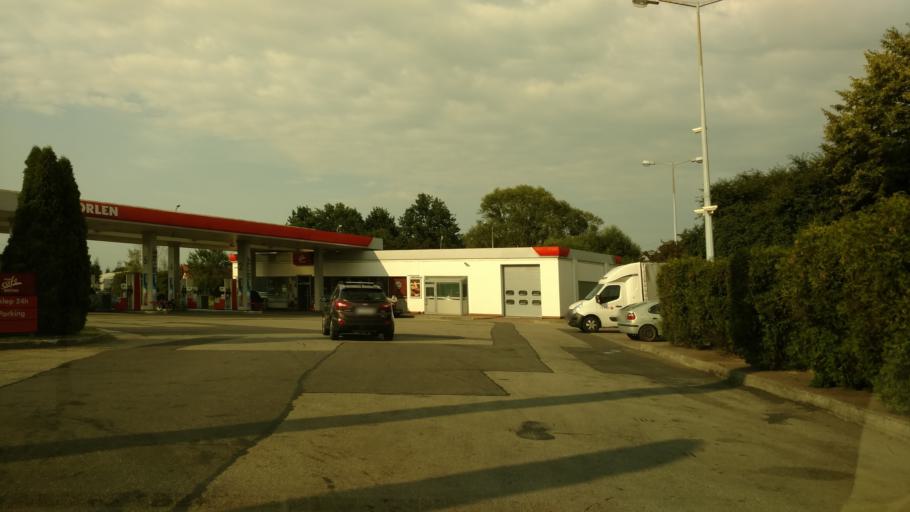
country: PL
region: Silesian Voivodeship
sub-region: Powiat pszczynski
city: Pszczyna
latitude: 49.9869
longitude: 18.9553
